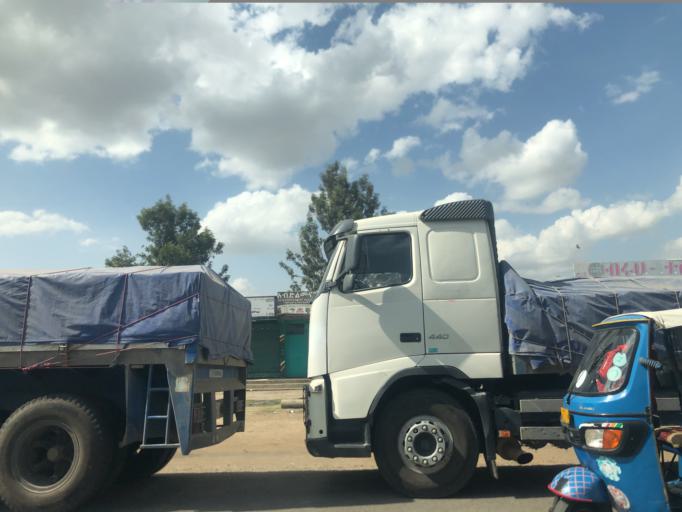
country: ET
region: Southern Nations, Nationalities, and People's Region
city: K'olito
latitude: 7.3063
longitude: 38.0915
